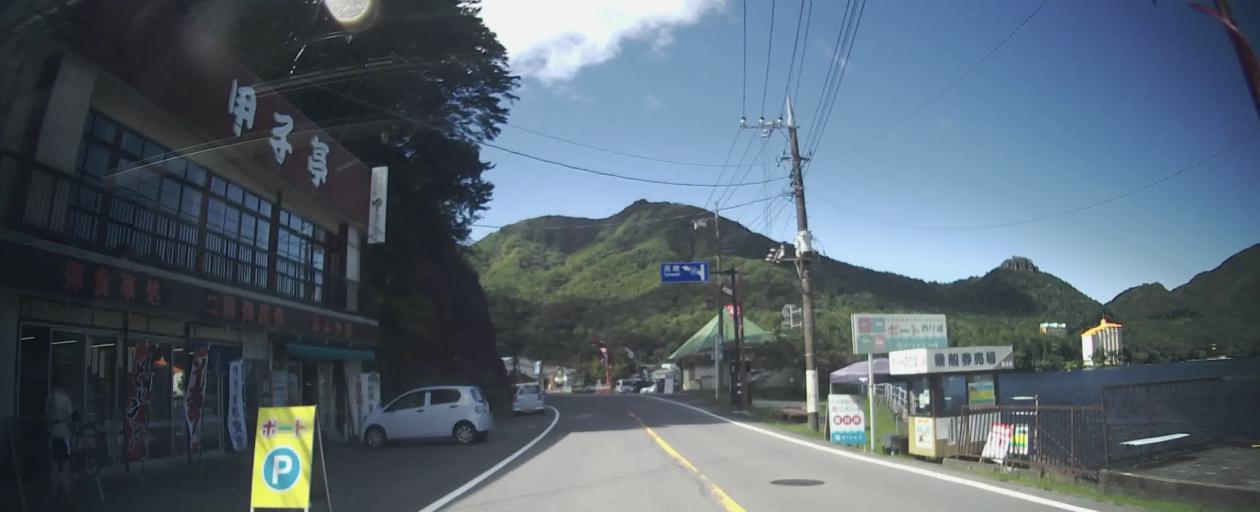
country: JP
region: Gunma
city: Nakanojomachi
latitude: 36.4678
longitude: 138.8631
